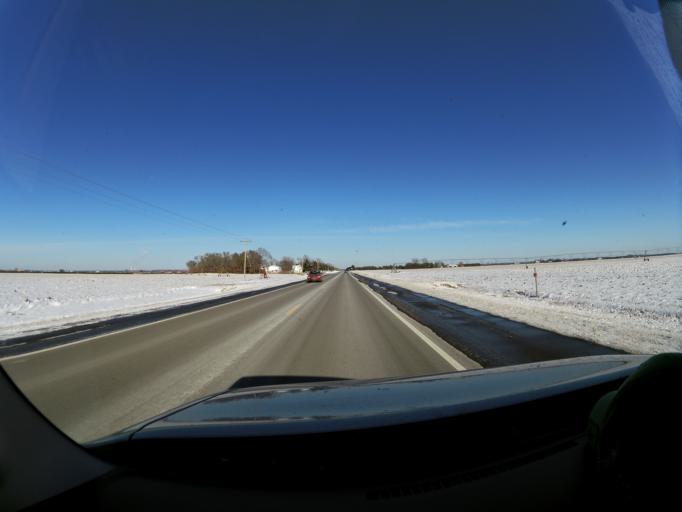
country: US
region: Minnesota
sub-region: Dakota County
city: Hastings
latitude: 44.6837
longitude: -92.9149
